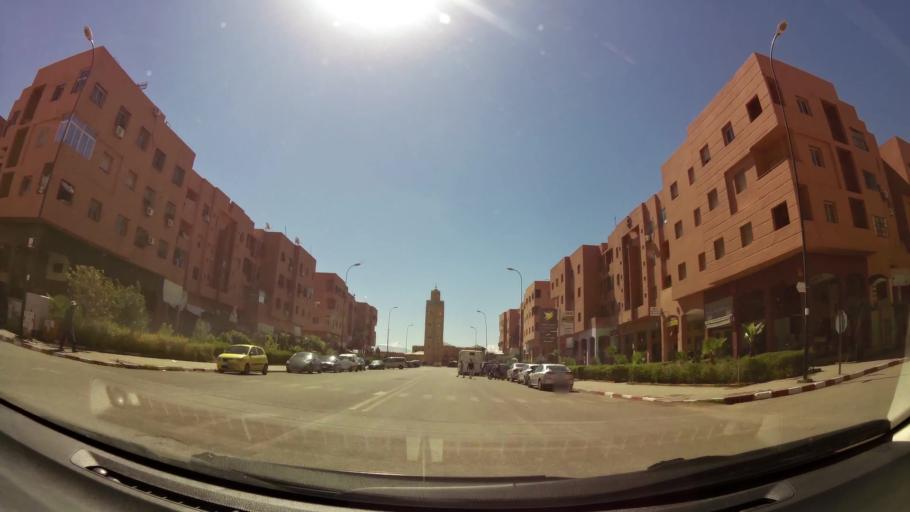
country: MA
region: Marrakech-Tensift-Al Haouz
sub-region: Marrakech
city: Marrakesh
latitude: 31.5739
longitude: -8.0569
